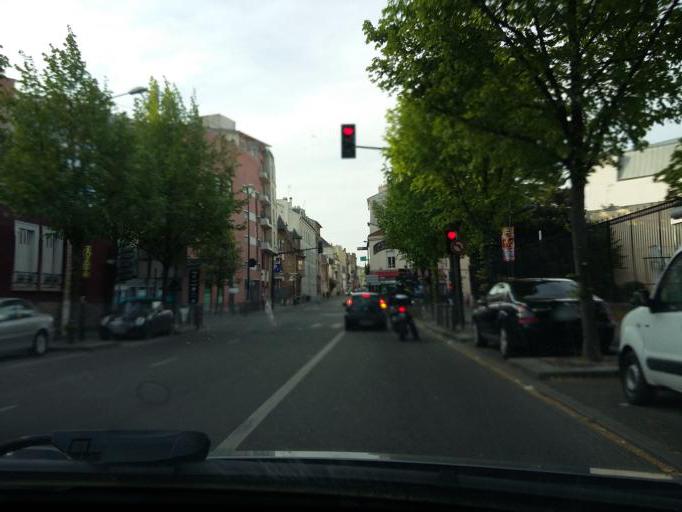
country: FR
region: Ile-de-France
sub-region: Departement du Val-d'Oise
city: Argenteuil
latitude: 48.9442
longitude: 2.2550
